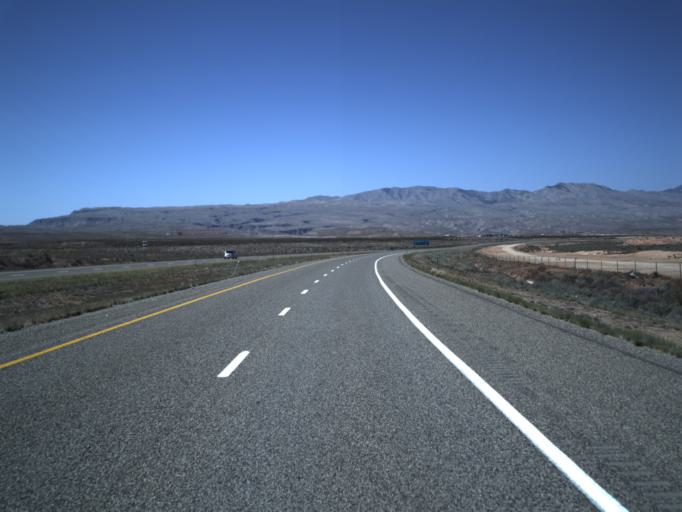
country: US
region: Utah
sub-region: Washington County
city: Saint George
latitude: 37.0012
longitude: -113.5738
